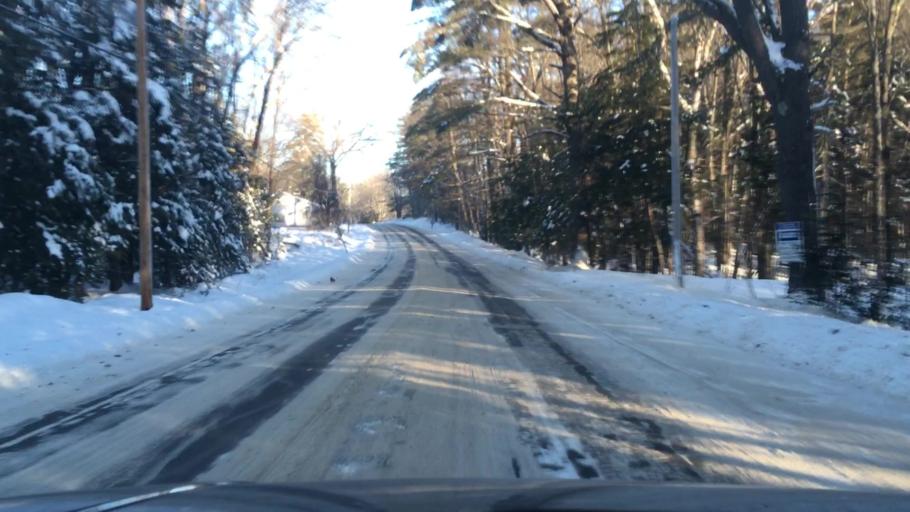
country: US
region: Maine
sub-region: Oxford County
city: Lovell
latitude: 44.1389
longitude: -70.9784
